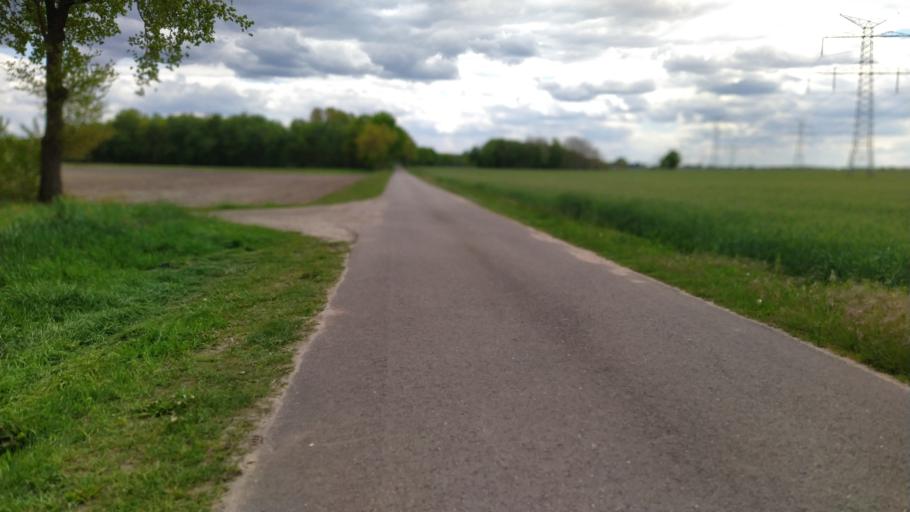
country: DE
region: Lower Saxony
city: Ahlerstedt
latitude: 53.3640
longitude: 9.3953
